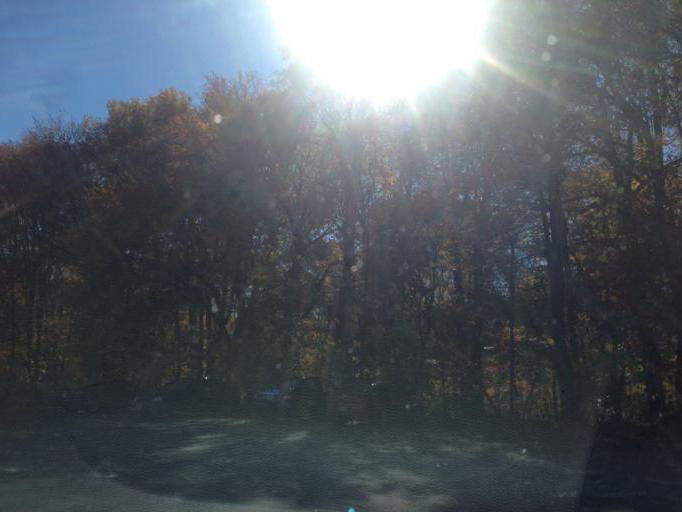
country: US
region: Maryland
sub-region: Howard County
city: Riverside
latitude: 39.2141
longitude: -76.8752
